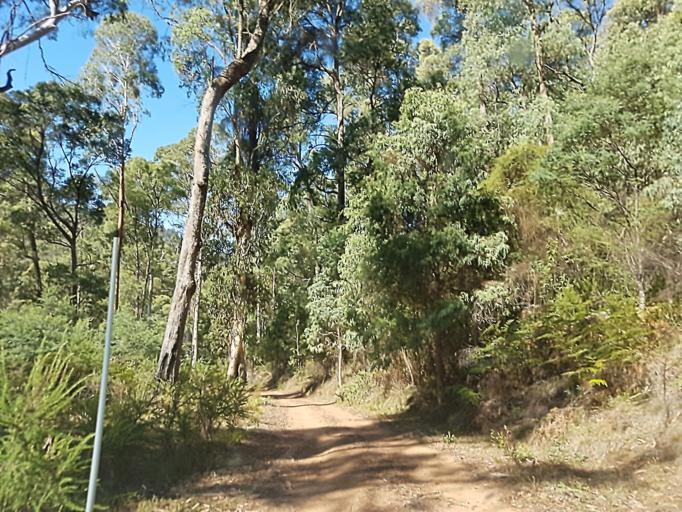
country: AU
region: Victoria
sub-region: Alpine
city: Mount Beauty
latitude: -36.9256
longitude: 147.0161
